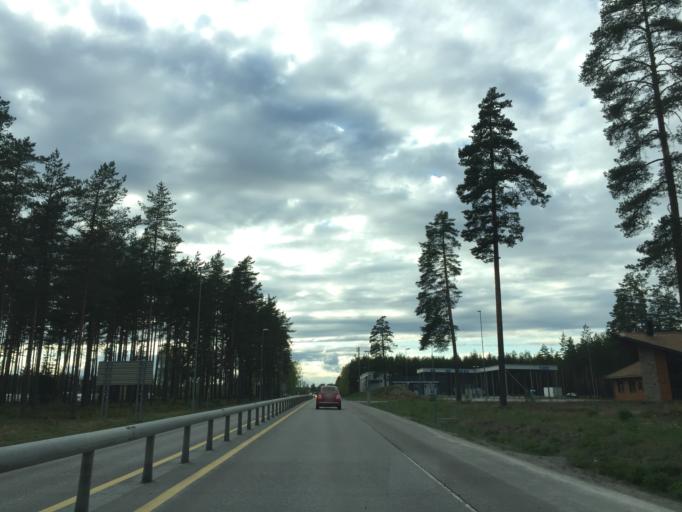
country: SE
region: Vaermland
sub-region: Eda Kommun
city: Charlottenberg
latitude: 59.9323
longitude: 12.2354
